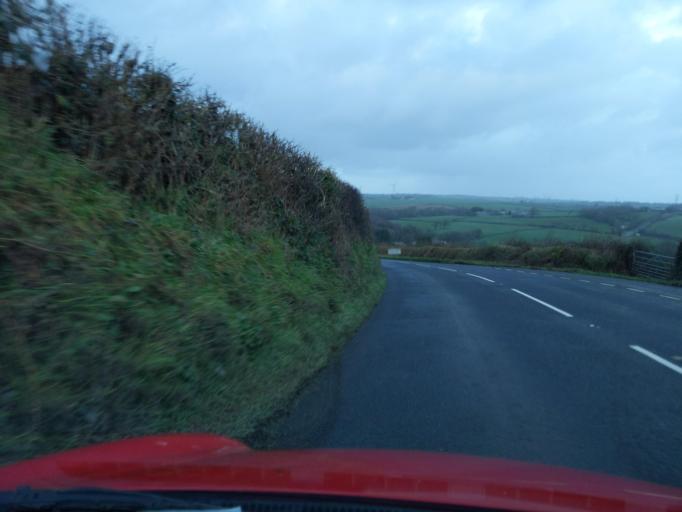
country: GB
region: England
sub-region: Devon
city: Holsworthy
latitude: 50.8855
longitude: -4.2810
